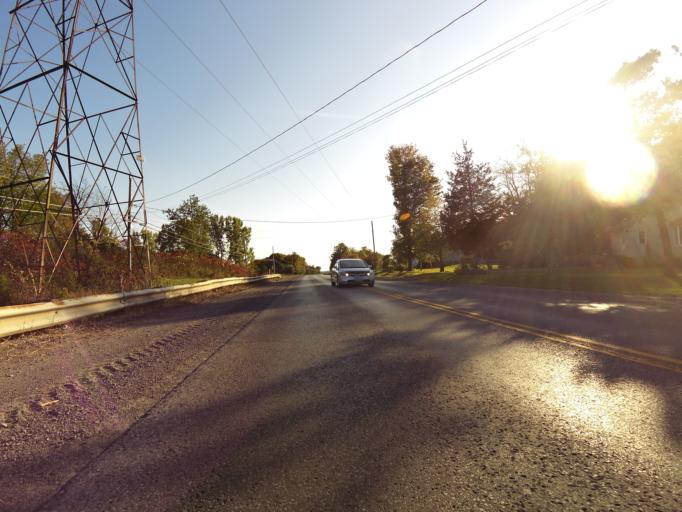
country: CA
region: Ontario
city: Kingston
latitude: 44.3284
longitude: -76.4580
